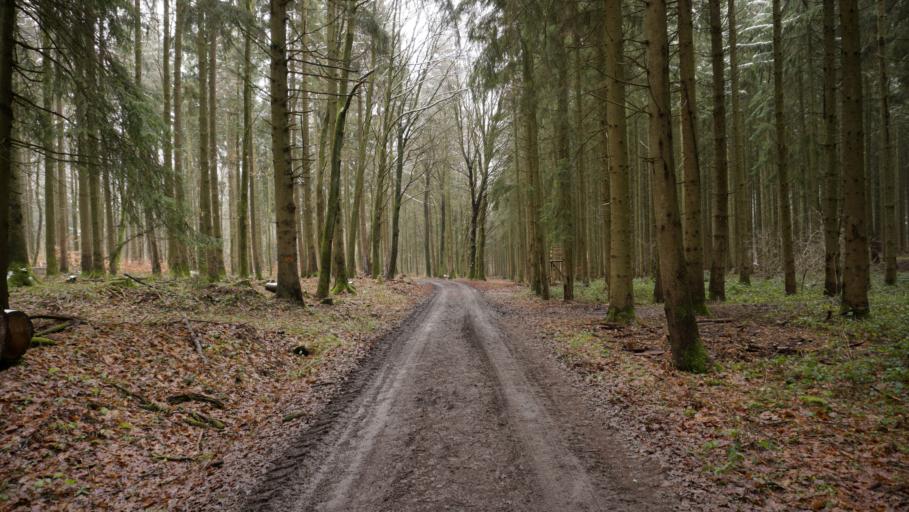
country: DE
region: Baden-Wuerttemberg
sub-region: Karlsruhe Region
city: Zwingenberg
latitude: 49.4069
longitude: 9.0291
